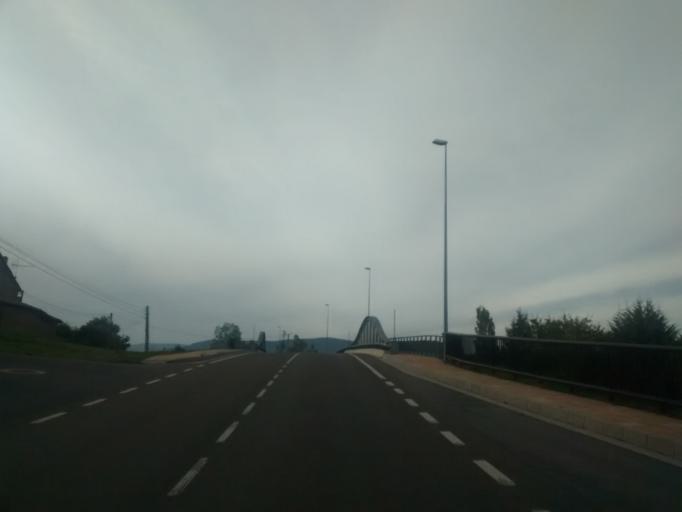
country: ES
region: Castille and Leon
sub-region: Provincia de Burgos
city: Arija
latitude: 42.9904
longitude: -3.9700
